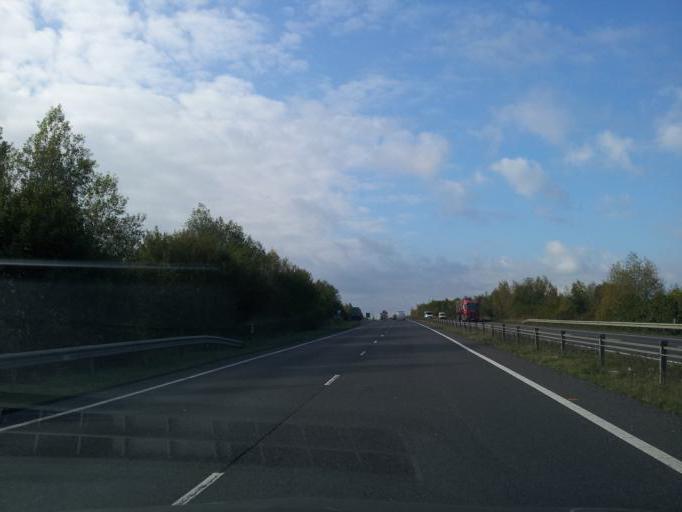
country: GB
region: England
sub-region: Northamptonshire
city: Brackley
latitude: 52.0576
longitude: -1.1067
